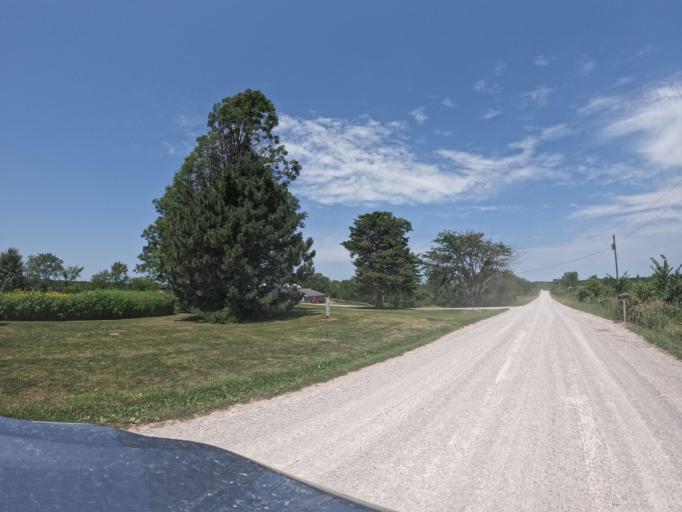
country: US
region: Iowa
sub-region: Appanoose County
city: Centerville
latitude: 40.7942
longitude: -92.9160
